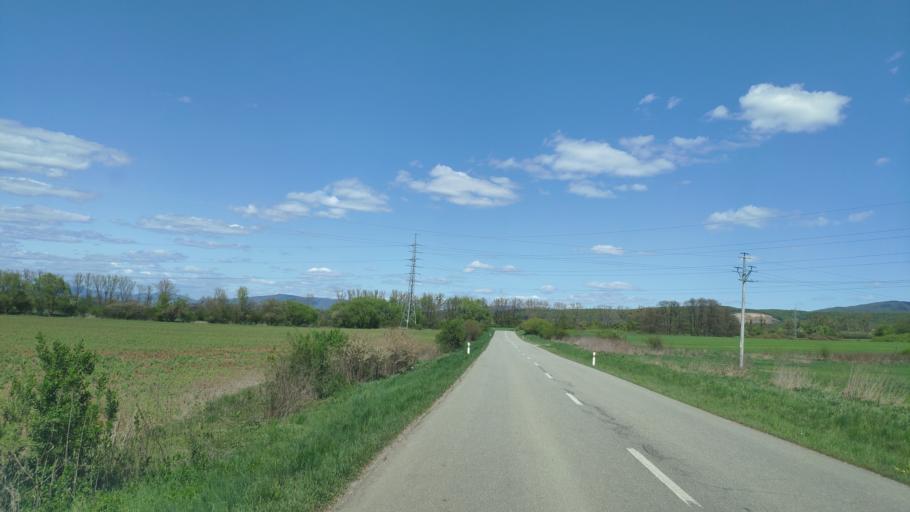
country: SK
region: Kosicky
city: Kosice
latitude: 48.6729
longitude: 21.4172
